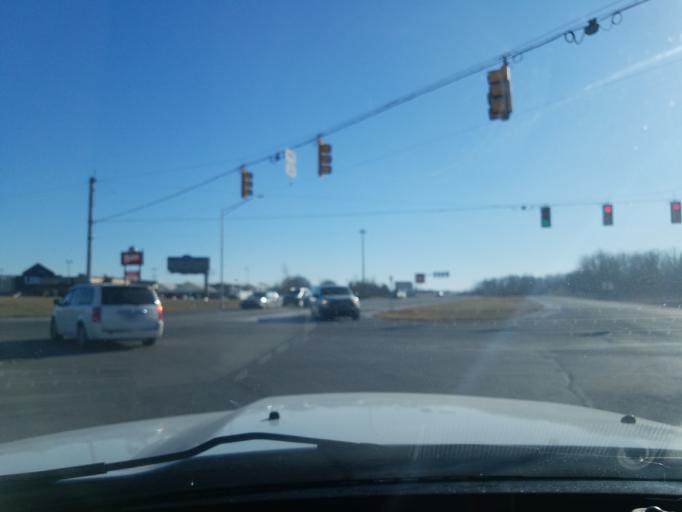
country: US
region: Indiana
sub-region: Lawrence County
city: Bedford
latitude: 38.8611
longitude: -86.5210
